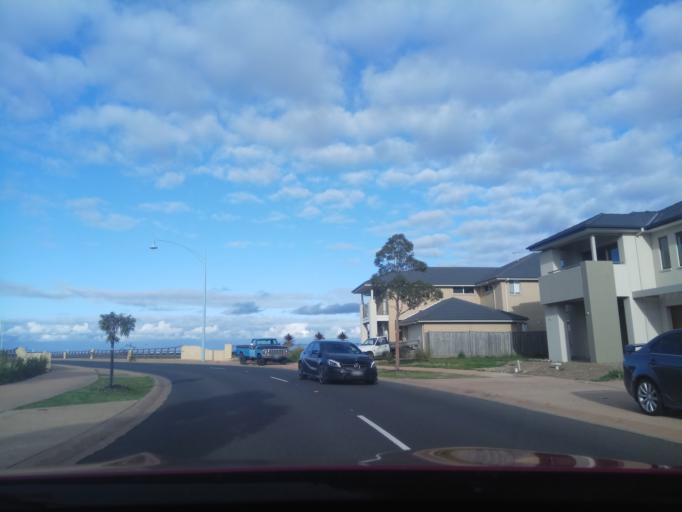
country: AU
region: Victoria
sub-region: Hobsons Bay
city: Altona Meadows
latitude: -37.9033
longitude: 144.7778
